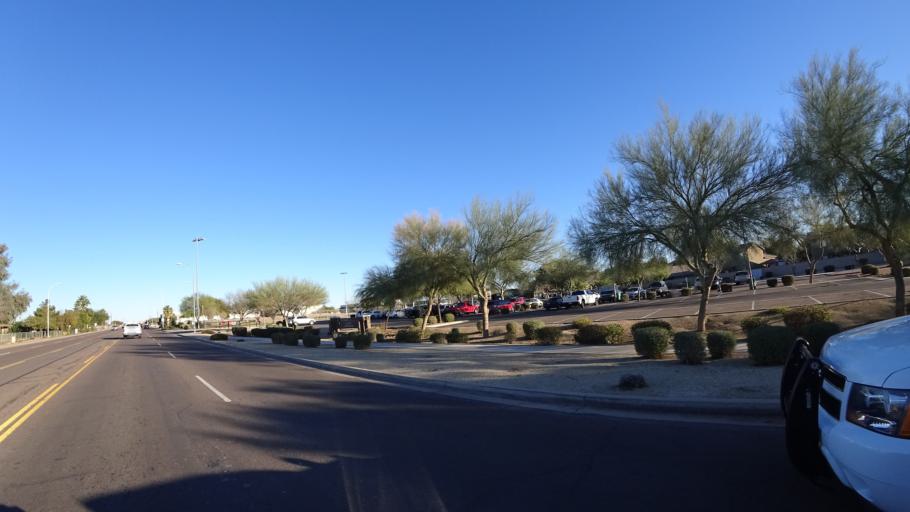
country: US
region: Arizona
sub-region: Maricopa County
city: Tolleson
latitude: 33.4511
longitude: -112.2462
